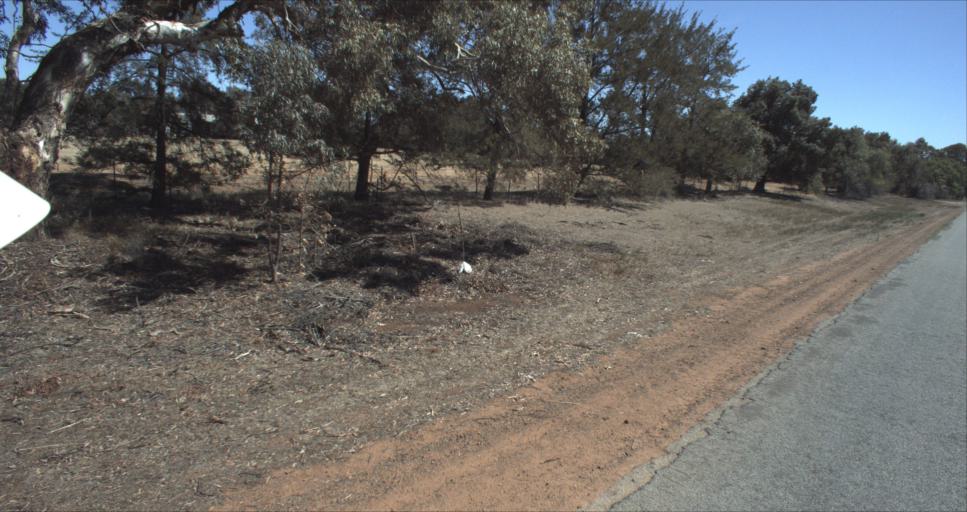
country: AU
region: New South Wales
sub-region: Leeton
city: Leeton
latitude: -34.5768
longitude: 146.3096
